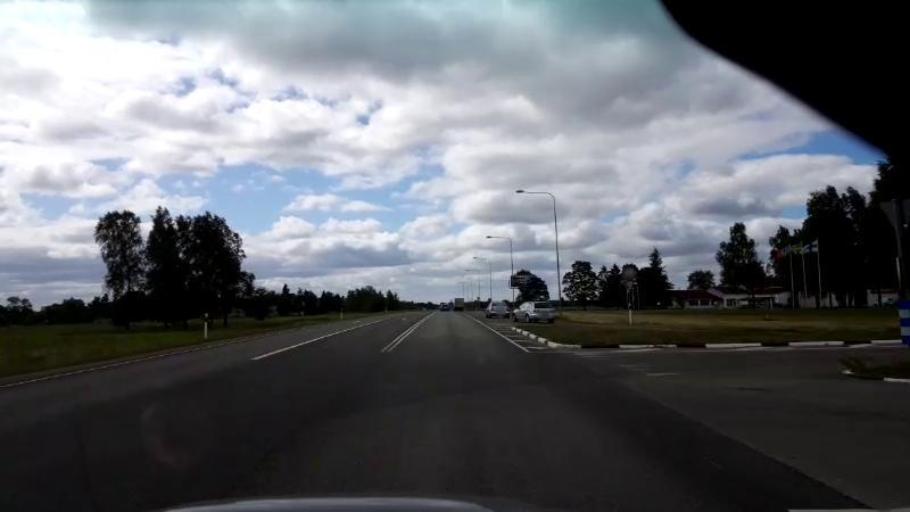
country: EE
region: Paernumaa
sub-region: Halinga vald
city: Parnu-Jaagupi
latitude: 58.5925
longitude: 24.5122
